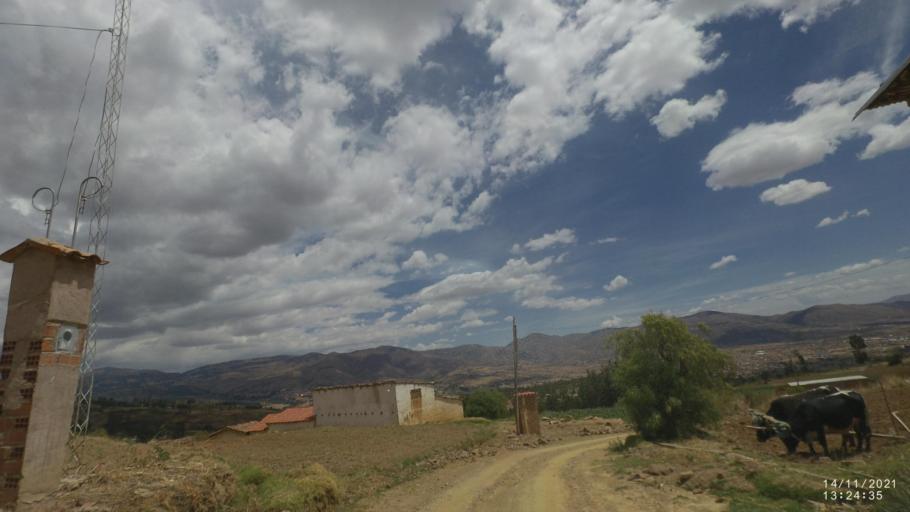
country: BO
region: Cochabamba
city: Colomi
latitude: -17.3782
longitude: -65.9803
